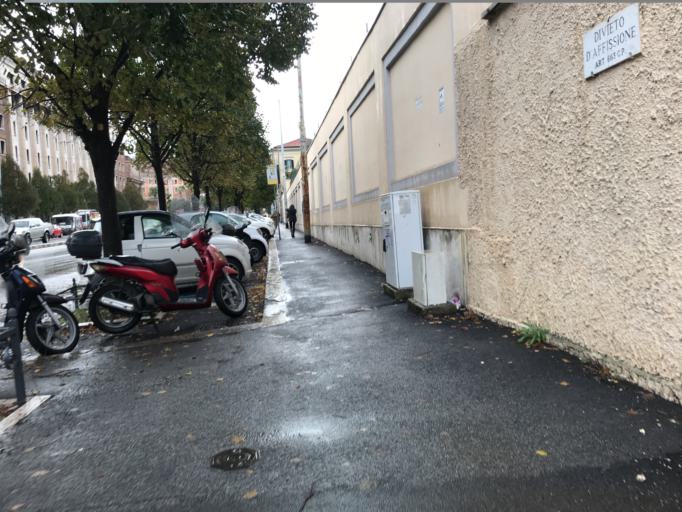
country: IT
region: Latium
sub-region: Citta metropolitana di Roma Capitale
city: Rome
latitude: 41.9064
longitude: 12.5056
